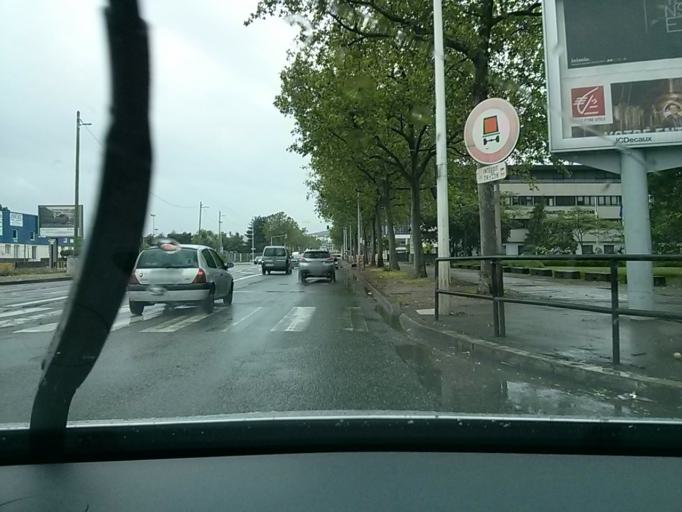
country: FR
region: Rhone-Alpes
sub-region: Departement du Rhone
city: Lyon
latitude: 45.7263
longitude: 4.8376
